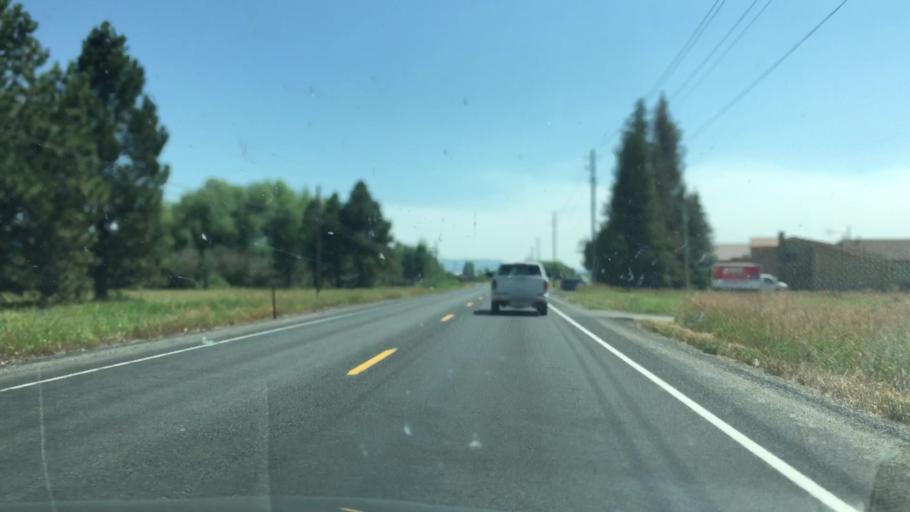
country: US
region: Idaho
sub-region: Valley County
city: McCall
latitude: 44.8483
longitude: -116.0900
